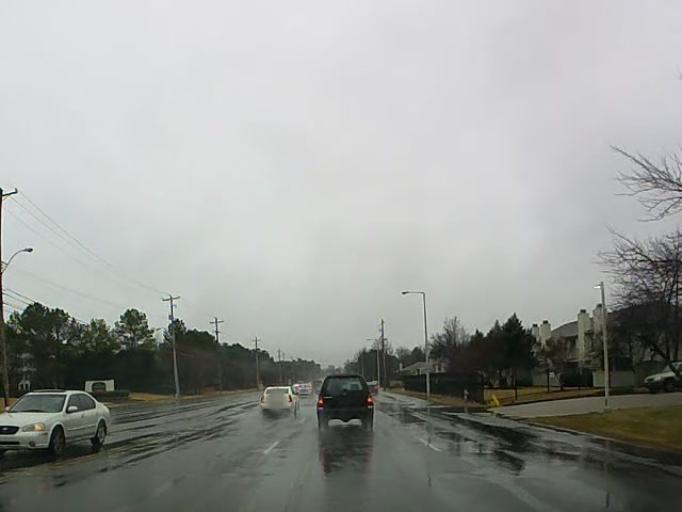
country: US
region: Tennessee
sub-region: Shelby County
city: Germantown
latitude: 35.0634
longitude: -89.8440
